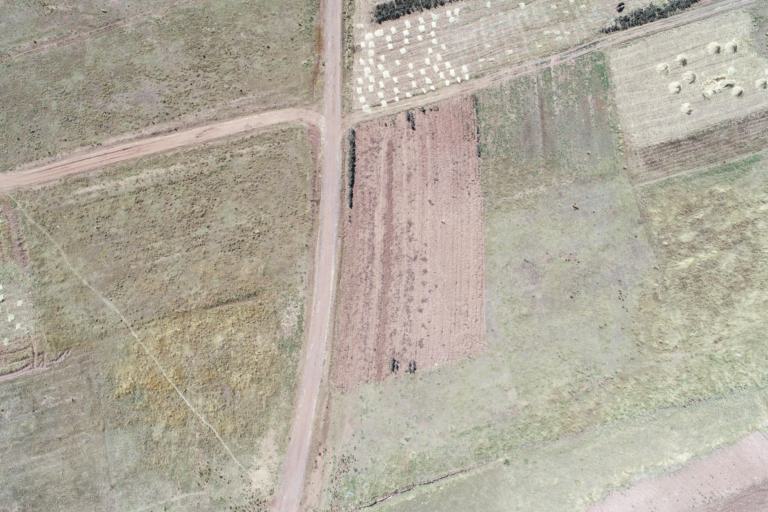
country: BO
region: La Paz
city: Tiahuanaco
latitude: -16.5928
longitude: -68.7717
